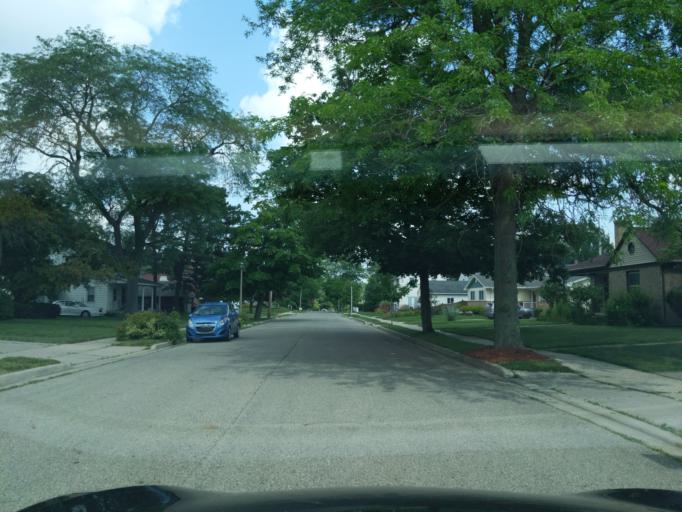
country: US
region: Michigan
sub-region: Ingham County
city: Lansing
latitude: 42.7189
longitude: -84.5761
